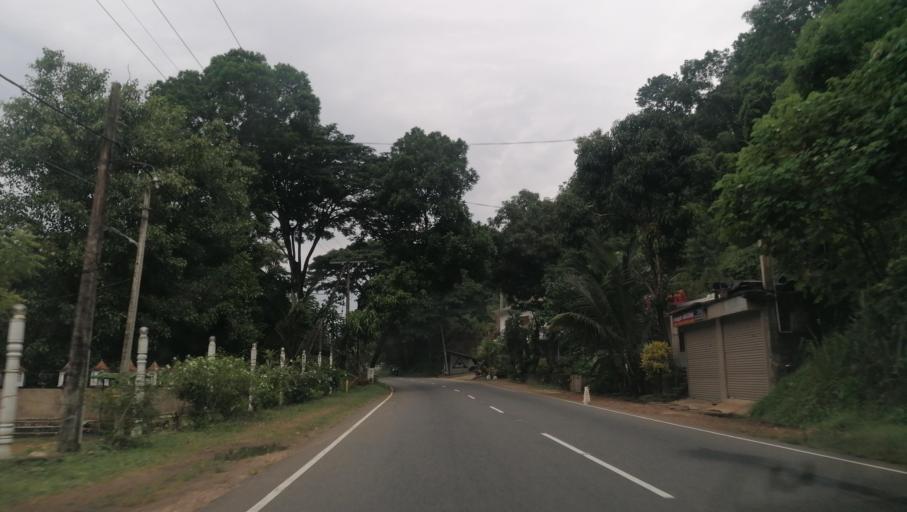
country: LK
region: Central
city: Kandy
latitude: 7.2459
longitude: 80.7245
